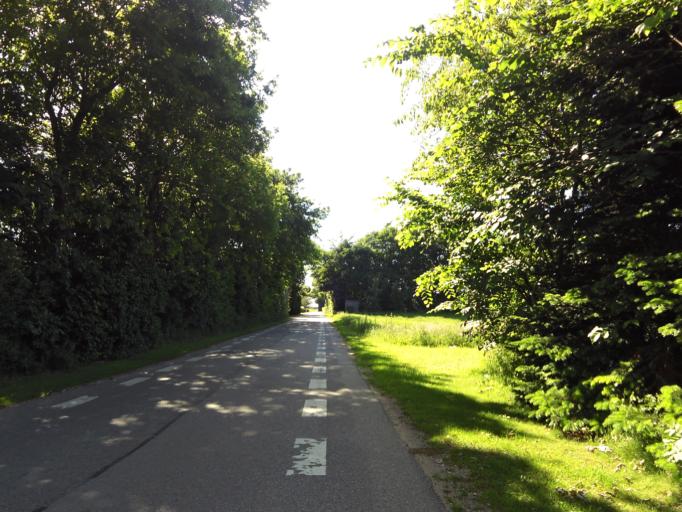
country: DK
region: South Denmark
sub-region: Aabenraa Kommune
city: Rodekro
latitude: 55.0707
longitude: 9.2966
